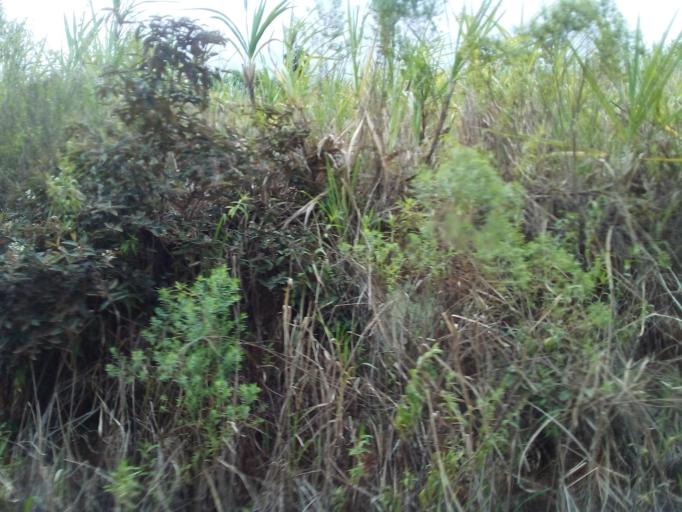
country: BR
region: Espirito Santo
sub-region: Ibiracu
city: Ibiracu
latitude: -19.7961
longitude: -40.3691
